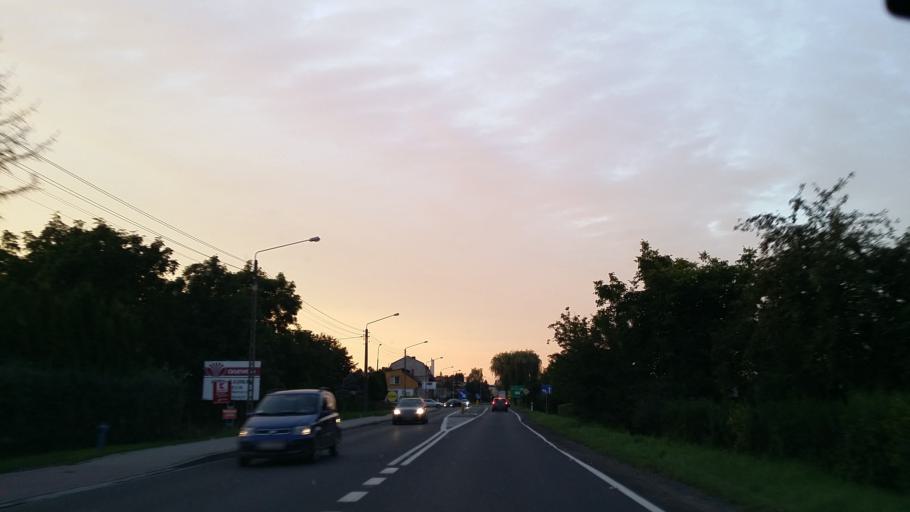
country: PL
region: Lesser Poland Voivodeship
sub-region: Powiat oswiecimski
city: Oswiecim
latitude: 50.0319
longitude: 19.2102
